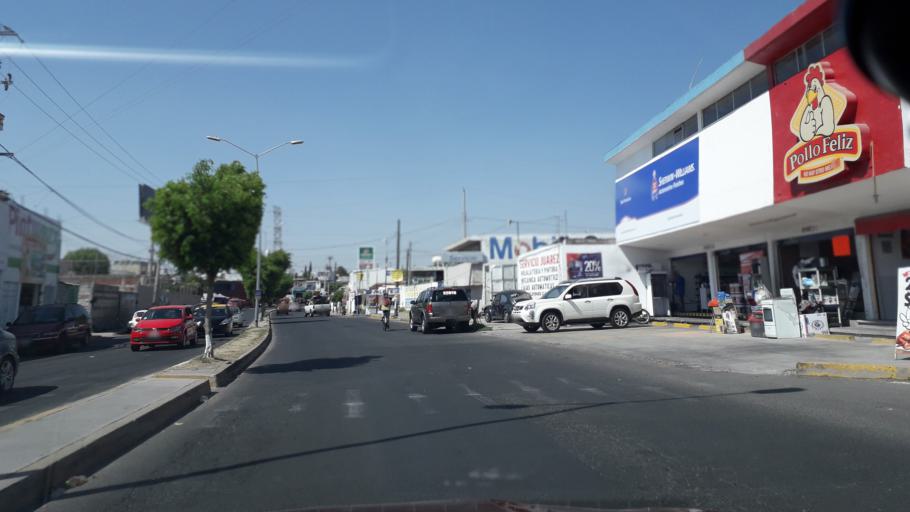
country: MX
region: Puebla
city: Puebla
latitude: 18.9924
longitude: -98.2134
